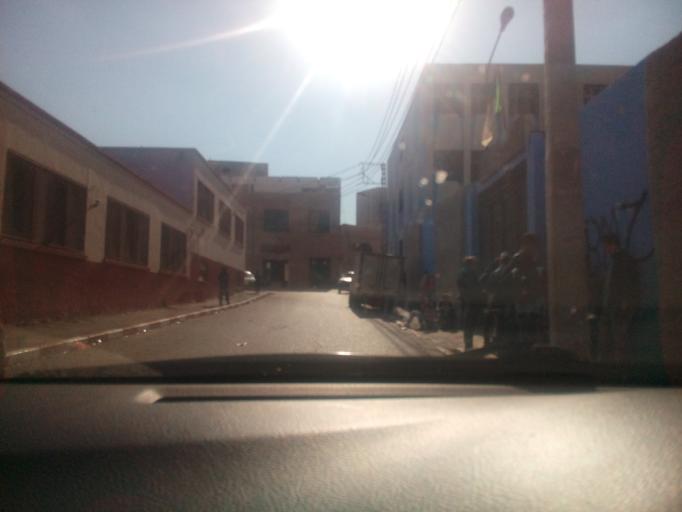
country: DZ
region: Oran
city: Oran
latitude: 35.7078
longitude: -0.6236
